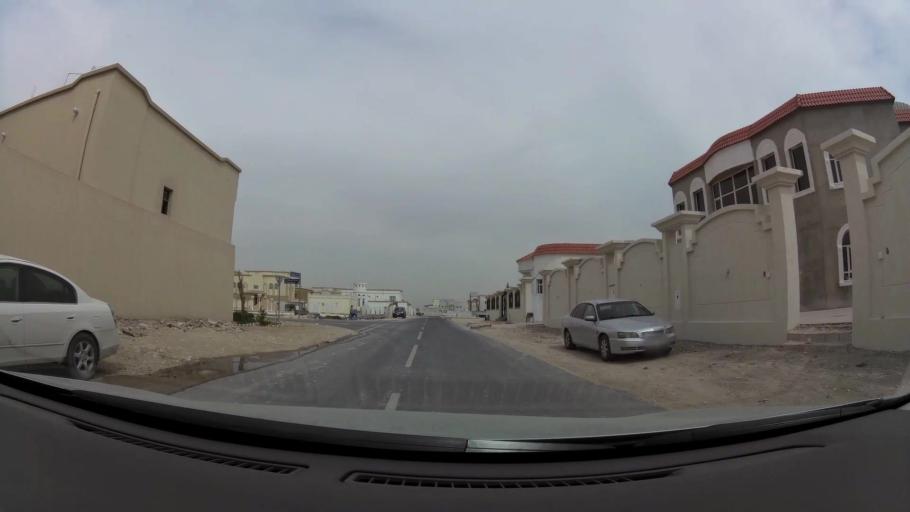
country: QA
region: Baladiyat ar Rayyan
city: Ar Rayyan
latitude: 25.2098
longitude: 51.4508
